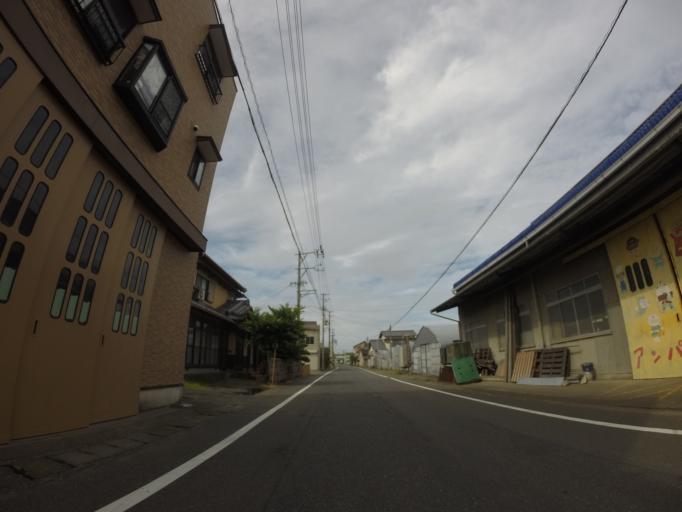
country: JP
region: Shizuoka
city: Sagara
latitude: 34.7233
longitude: 138.2172
